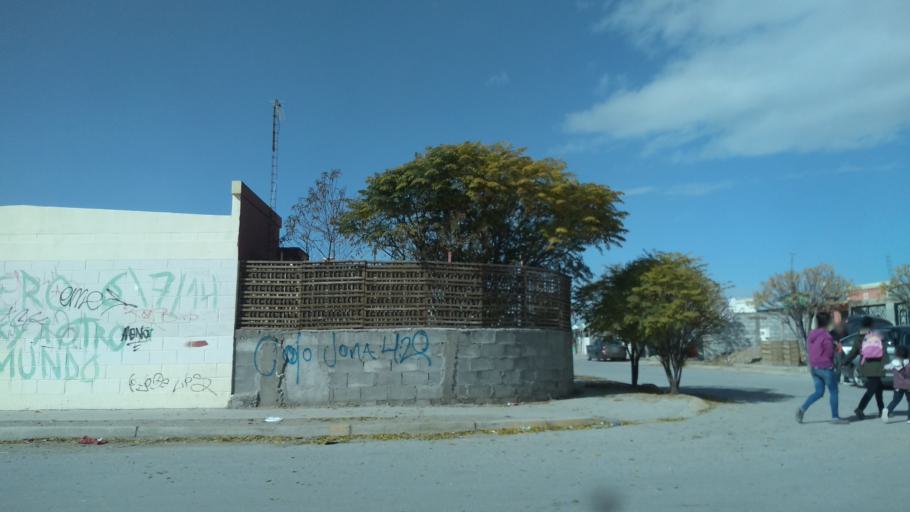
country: US
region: Texas
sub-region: El Paso County
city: San Elizario
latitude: 31.5665
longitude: -106.3333
